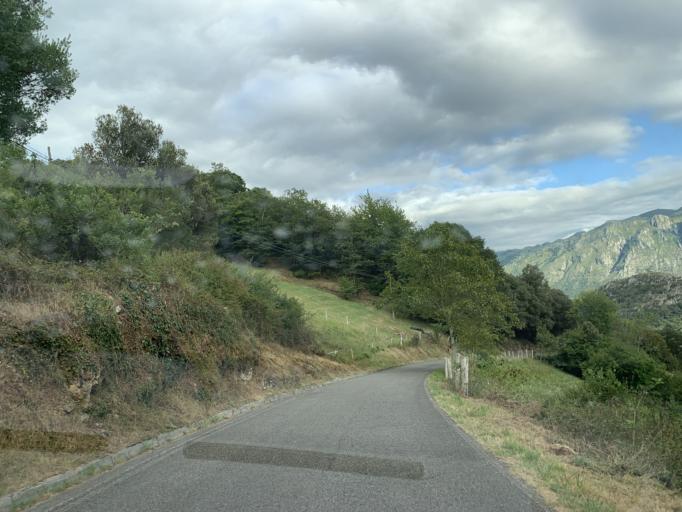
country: ES
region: Asturias
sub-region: Province of Asturias
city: Carrena
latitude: 43.3240
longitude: -4.8590
